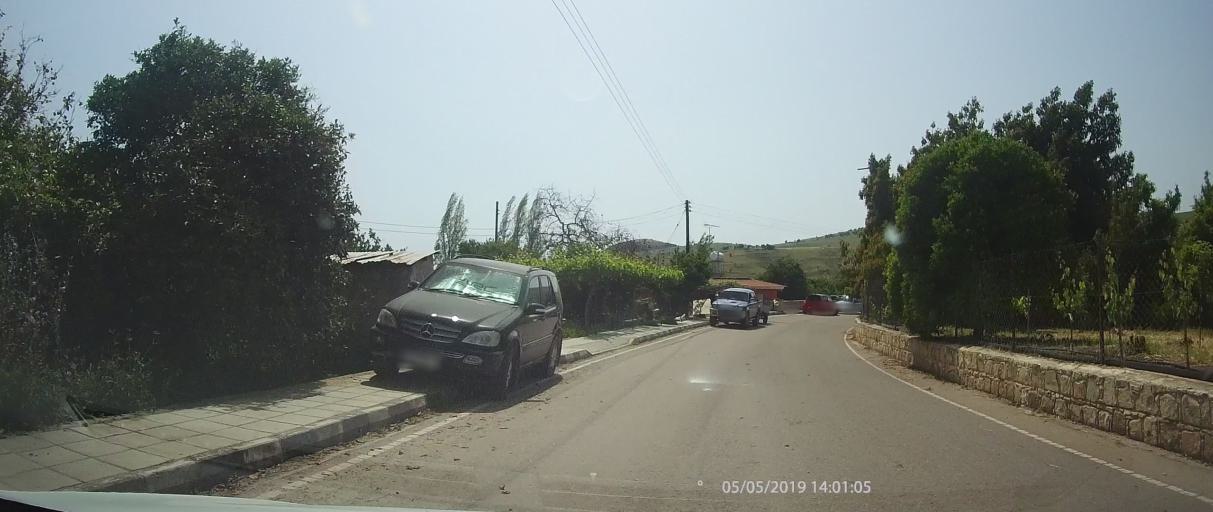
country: CY
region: Limassol
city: Pissouri
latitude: 34.7781
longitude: 32.6525
